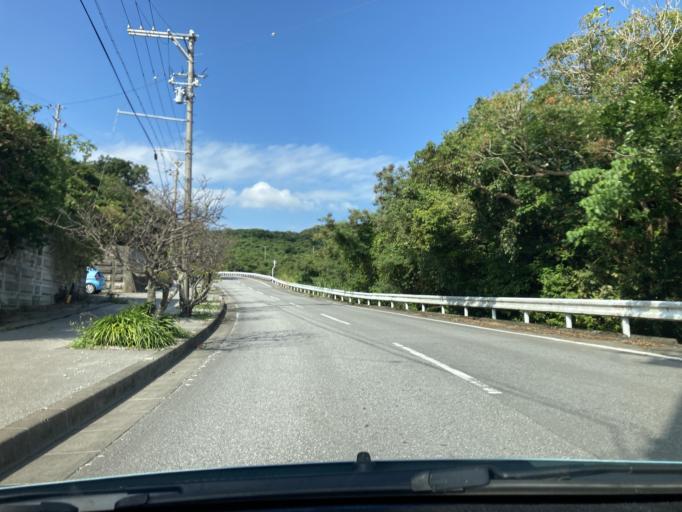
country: JP
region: Okinawa
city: Ginowan
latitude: 26.2794
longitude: 127.7991
